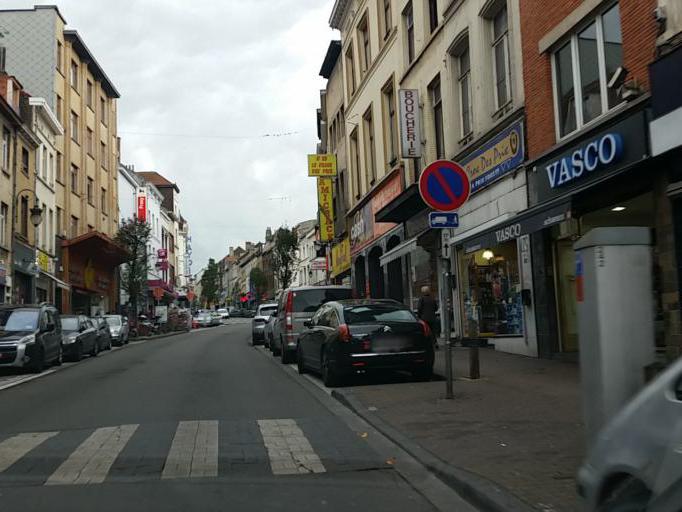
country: BE
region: Brussels Capital
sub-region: Bruxelles-Capitale
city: Brussels
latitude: 50.8298
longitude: 4.3444
